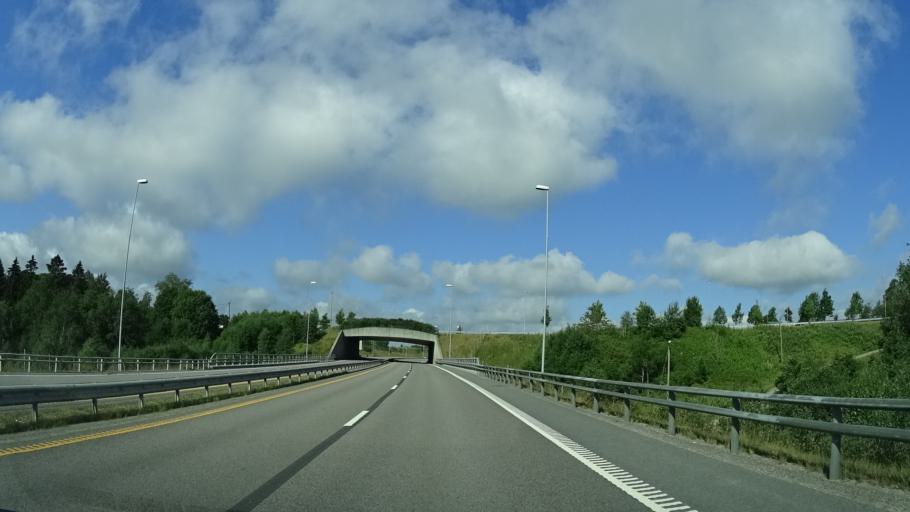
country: NO
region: Ostfold
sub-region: Eidsberg
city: Mysen
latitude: 59.5773
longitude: 11.2624
